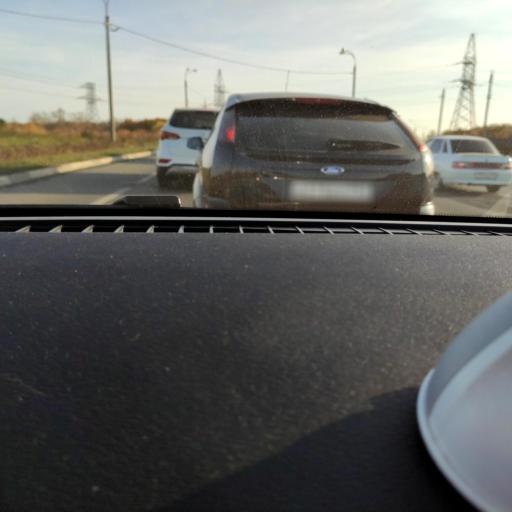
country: RU
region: Samara
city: Samara
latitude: 53.1338
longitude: 50.1735
